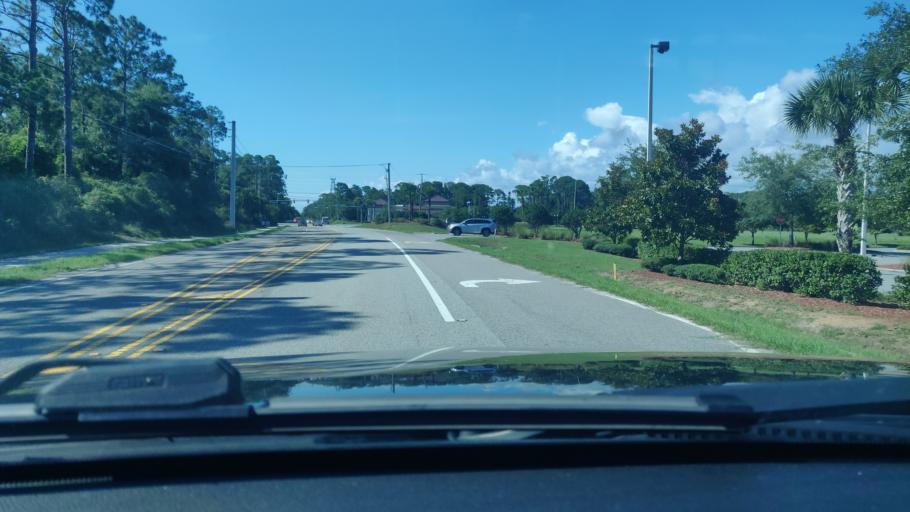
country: US
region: Florida
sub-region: Flagler County
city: Flagler Beach
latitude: 29.4785
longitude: -81.1465
